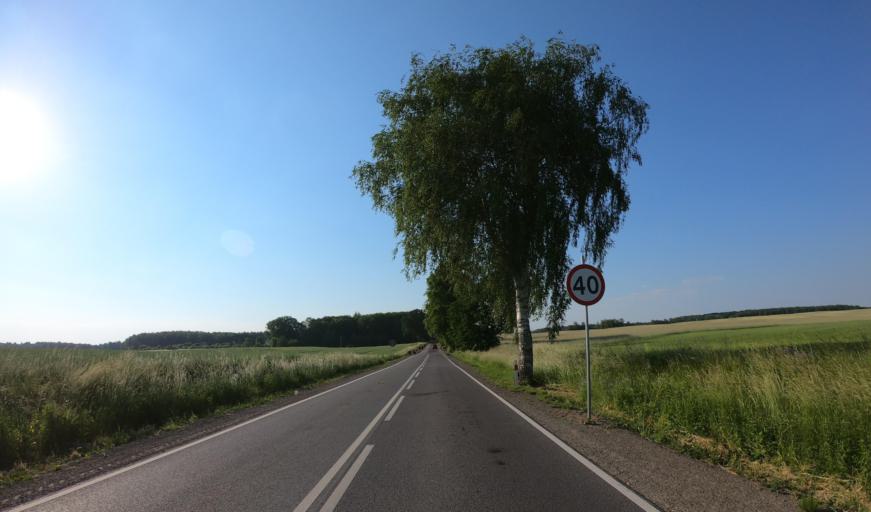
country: PL
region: West Pomeranian Voivodeship
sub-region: Powiat lobeski
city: Dobra
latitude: 53.5514
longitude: 15.3086
